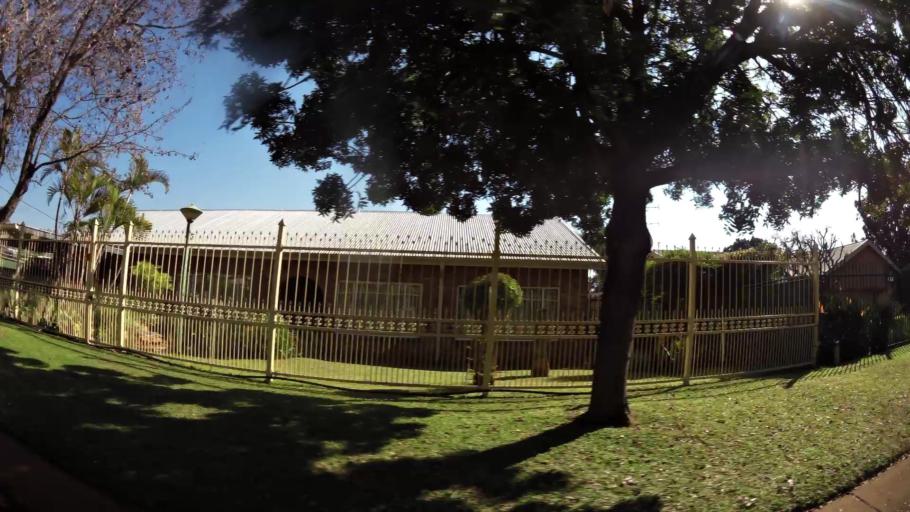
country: ZA
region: Gauteng
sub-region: City of Tshwane Metropolitan Municipality
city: Pretoria
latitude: -25.6759
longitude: 28.2095
